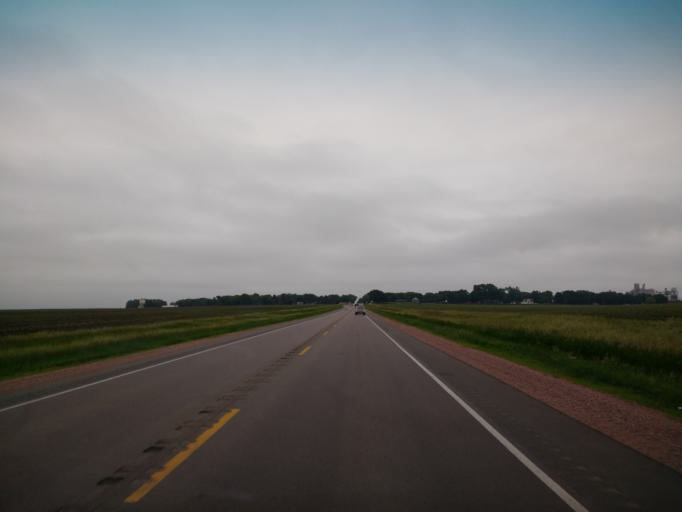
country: US
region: Iowa
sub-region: O'Brien County
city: Sanborn
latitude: 43.1861
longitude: -95.6731
